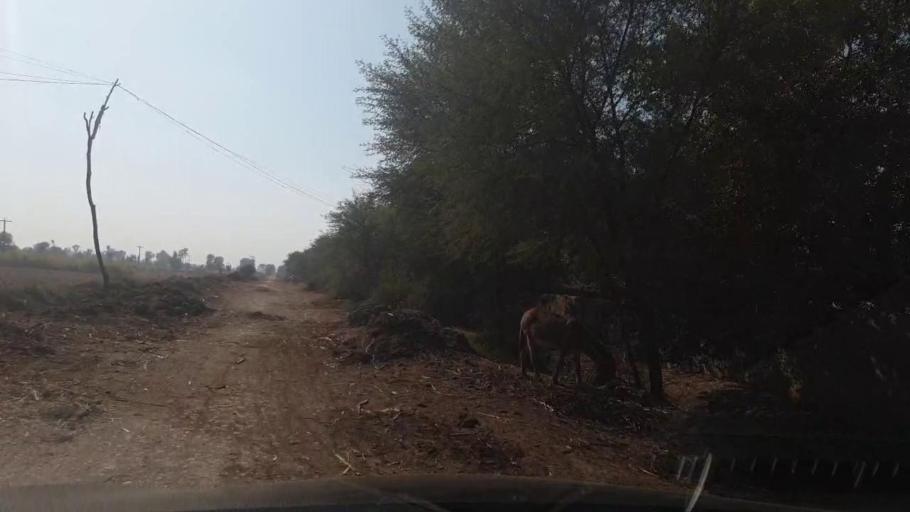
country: PK
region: Sindh
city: Ubauro
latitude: 28.1513
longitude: 69.6928
